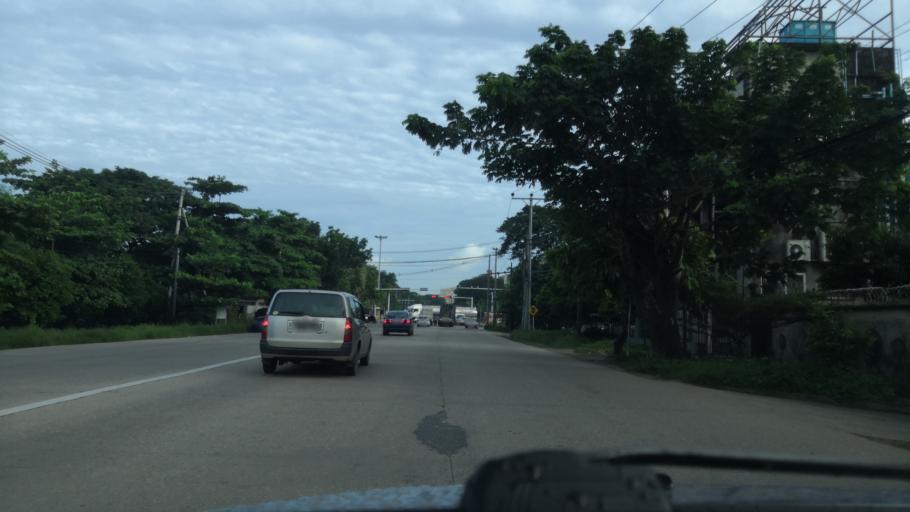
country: MM
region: Yangon
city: Yangon
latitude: 16.8935
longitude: 96.1579
